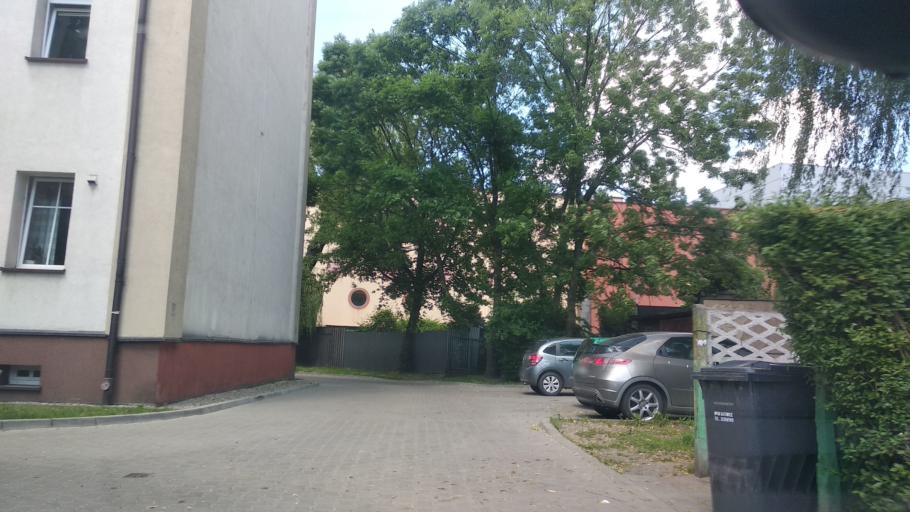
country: PL
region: Silesian Voivodeship
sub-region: Katowice
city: Katowice
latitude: 50.2618
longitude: 19.0053
